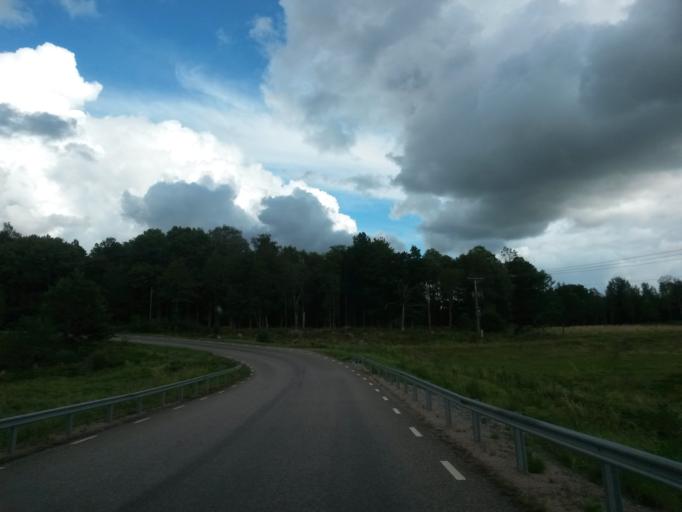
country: SE
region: Vaestra Goetaland
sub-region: Vargarda Kommun
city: Vargarda
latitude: 57.9889
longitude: 12.7982
